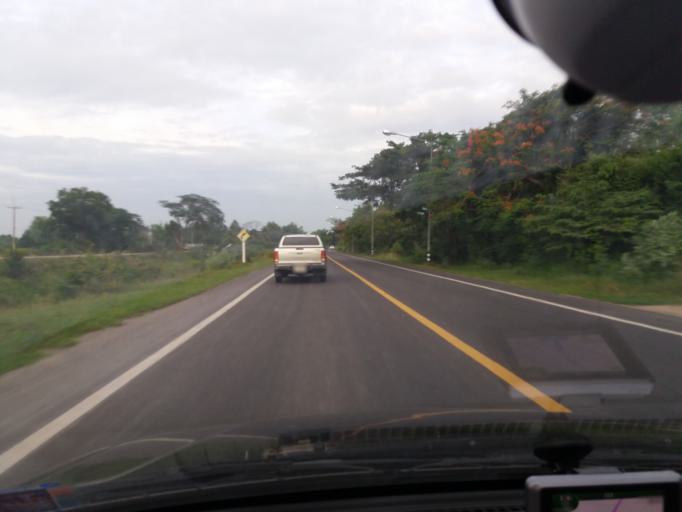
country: TH
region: Suphan Buri
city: Don Chedi
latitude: 14.5238
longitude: 99.9275
